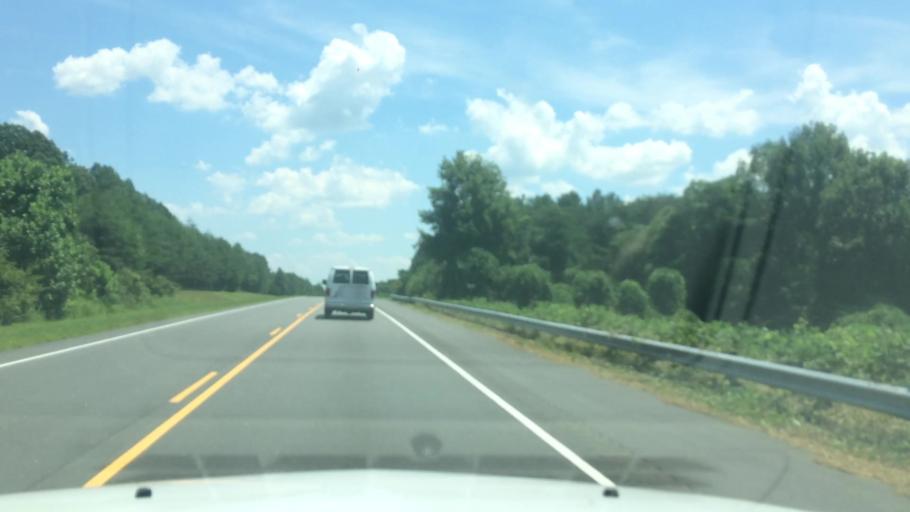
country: US
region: North Carolina
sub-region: Alexander County
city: Stony Point
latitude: 35.8108
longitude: -80.9743
